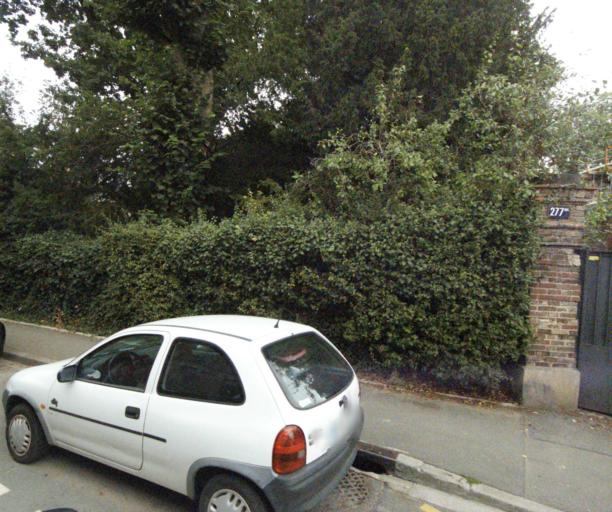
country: FR
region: Nord-Pas-de-Calais
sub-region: Departement du Nord
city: La Madeleine
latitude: 50.6477
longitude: 3.0845
